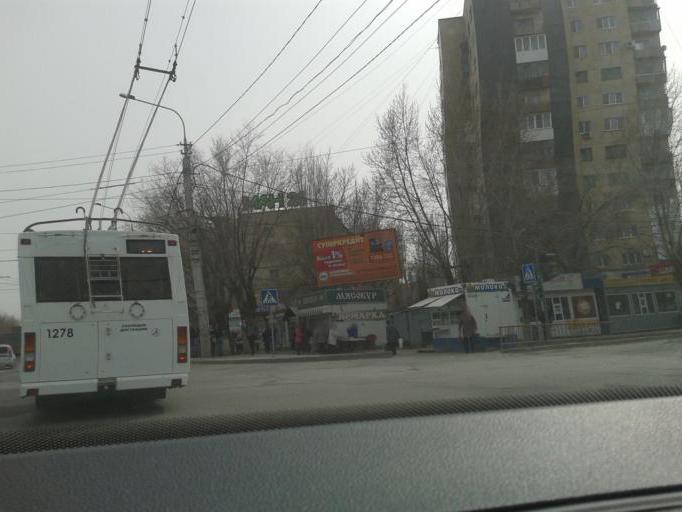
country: RU
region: Volgograd
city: Volgograd
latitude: 48.7418
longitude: 44.4901
